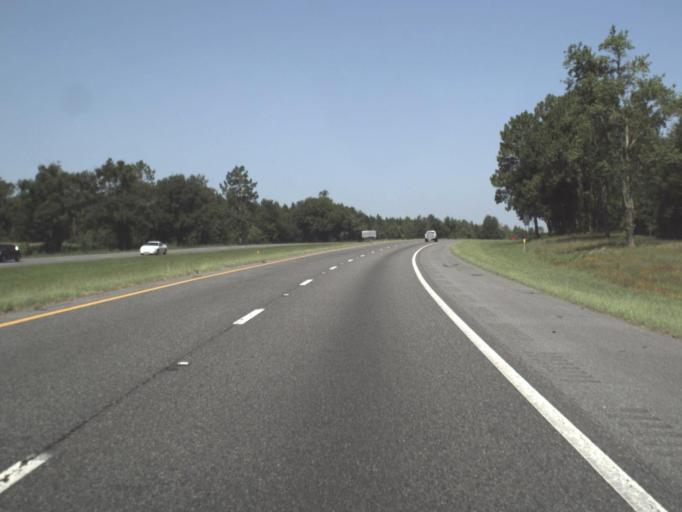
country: US
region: Florida
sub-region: Suwannee County
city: Live Oak
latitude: 30.3373
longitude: -83.1040
